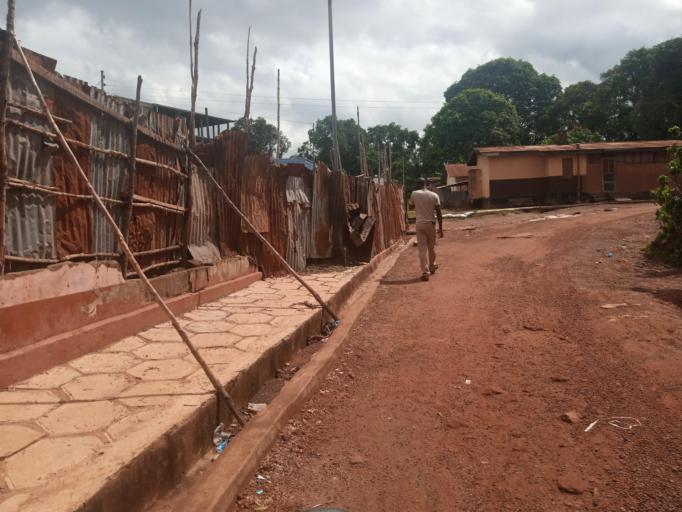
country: SL
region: Southern Province
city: Bo
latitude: 7.9712
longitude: -11.7421
